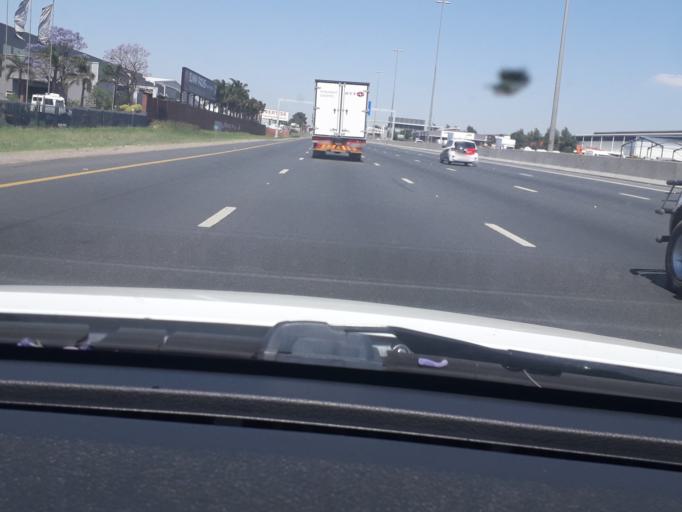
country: ZA
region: Gauteng
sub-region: Ekurhuleni Metropolitan Municipality
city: Boksburg
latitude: -26.1760
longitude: 28.2250
